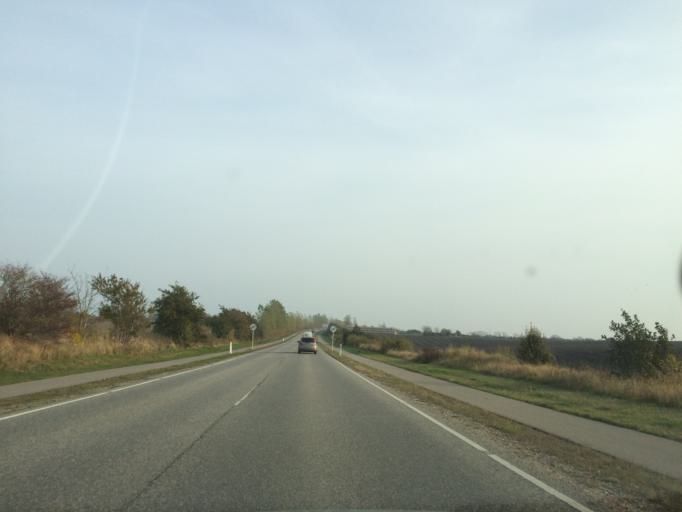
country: DK
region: Zealand
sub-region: Odsherred Kommune
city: Asnaes
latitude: 55.9763
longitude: 11.3361
